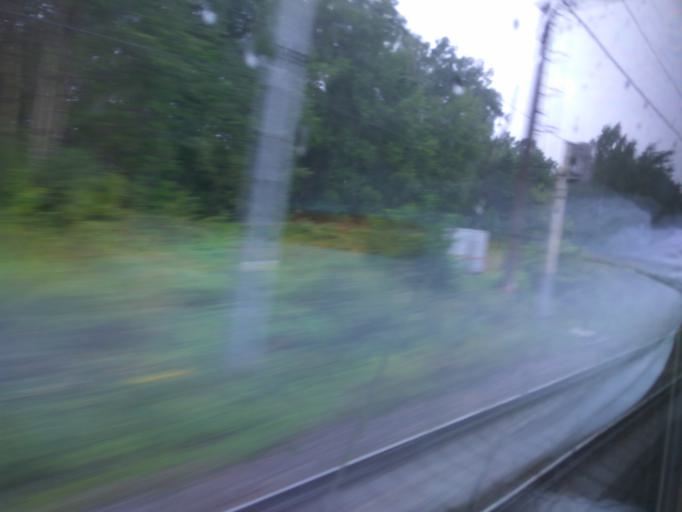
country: RU
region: Moskovskaya
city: Kashira
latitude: 54.8461
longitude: 38.2289
